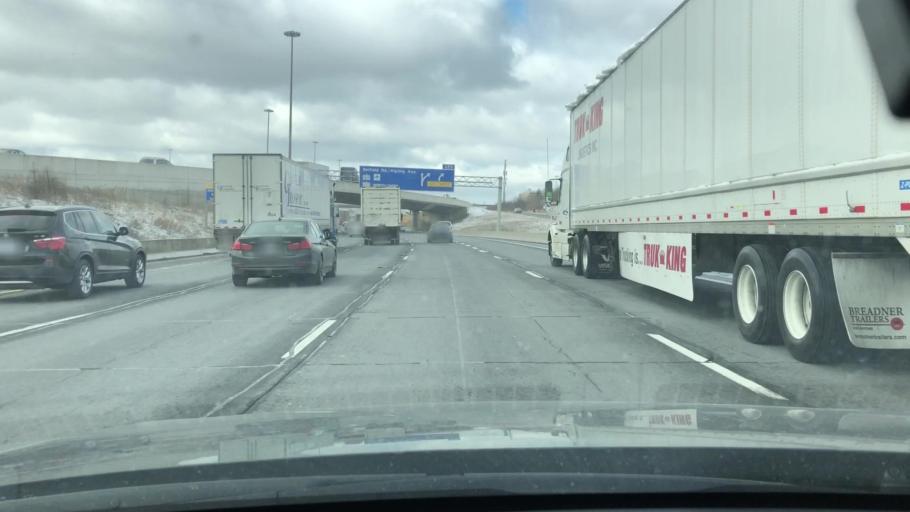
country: CA
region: Ontario
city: Etobicoke
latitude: 43.7129
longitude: -79.5446
